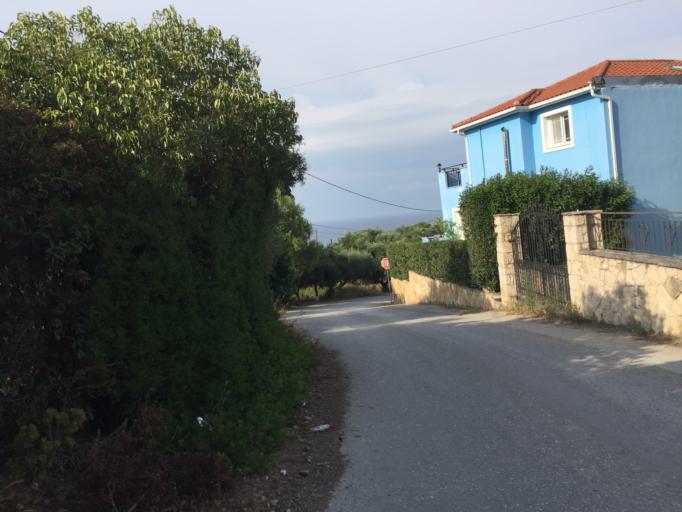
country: GR
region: Ionian Islands
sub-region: Nomos Zakynthou
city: Vanaton
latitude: 37.8134
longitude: 20.8621
